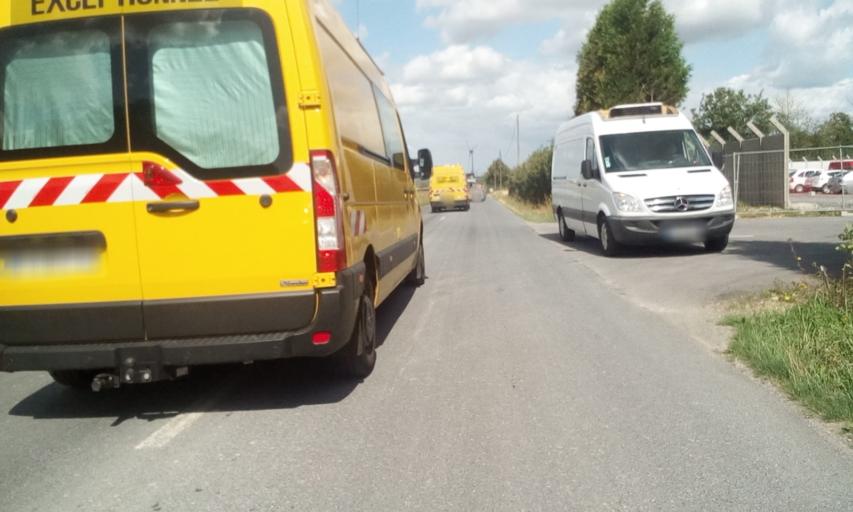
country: FR
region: Lower Normandy
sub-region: Departement du Calvados
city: Cagny
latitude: 49.1113
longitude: -0.2633
